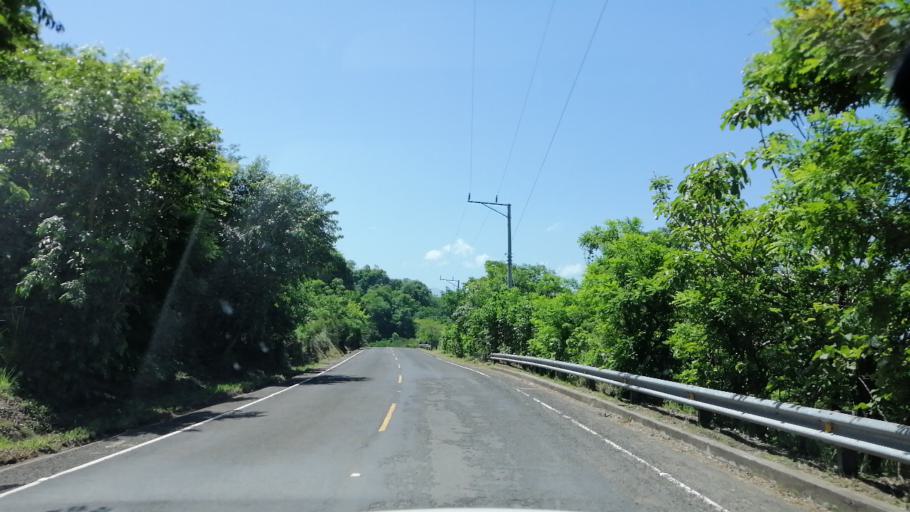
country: SV
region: San Miguel
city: Sesori
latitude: 13.8054
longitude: -88.3853
